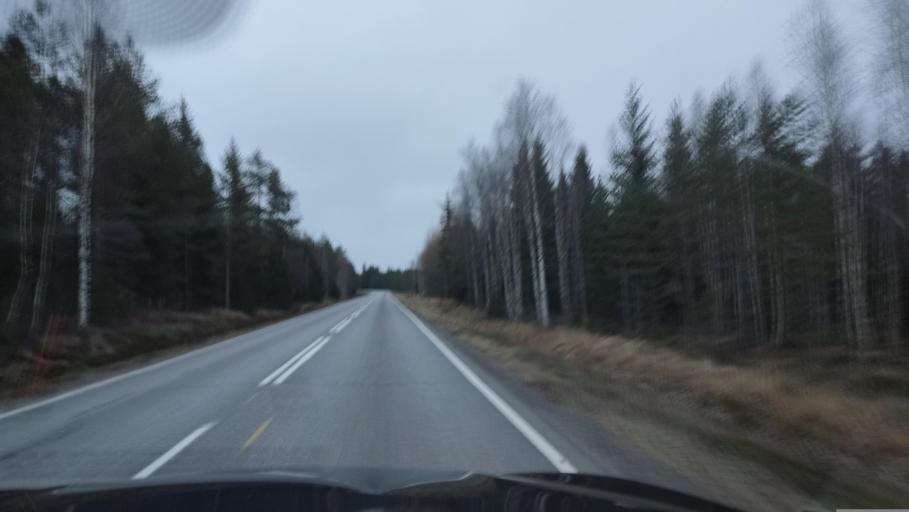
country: FI
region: Southern Ostrobothnia
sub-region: Suupohja
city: Isojoki
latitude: 62.3393
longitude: 21.9398
